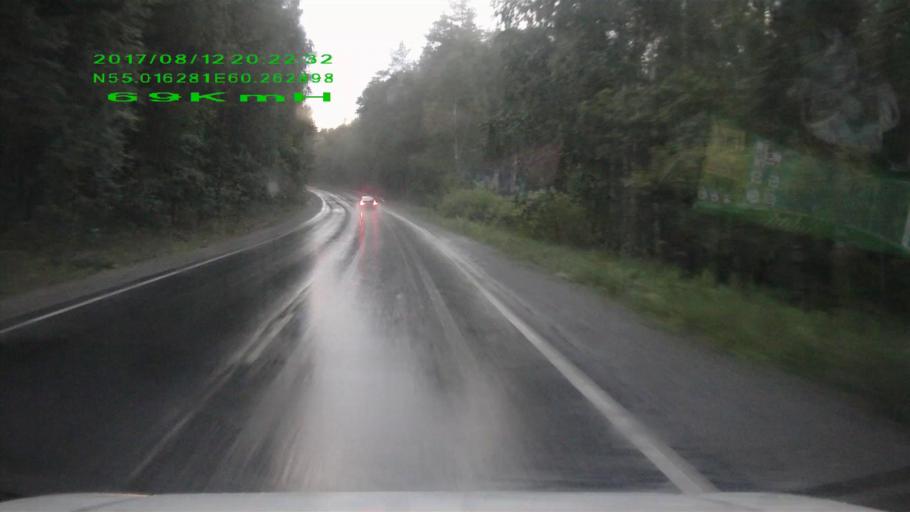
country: RU
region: Chelyabinsk
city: Chebarkul'
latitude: 55.0164
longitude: 60.2627
